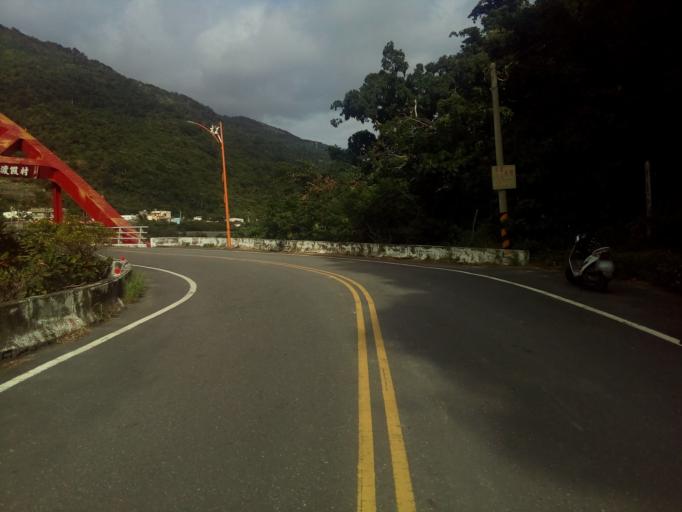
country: TW
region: Taiwan
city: Taitung City
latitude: 22.5280
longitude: 120.9399
